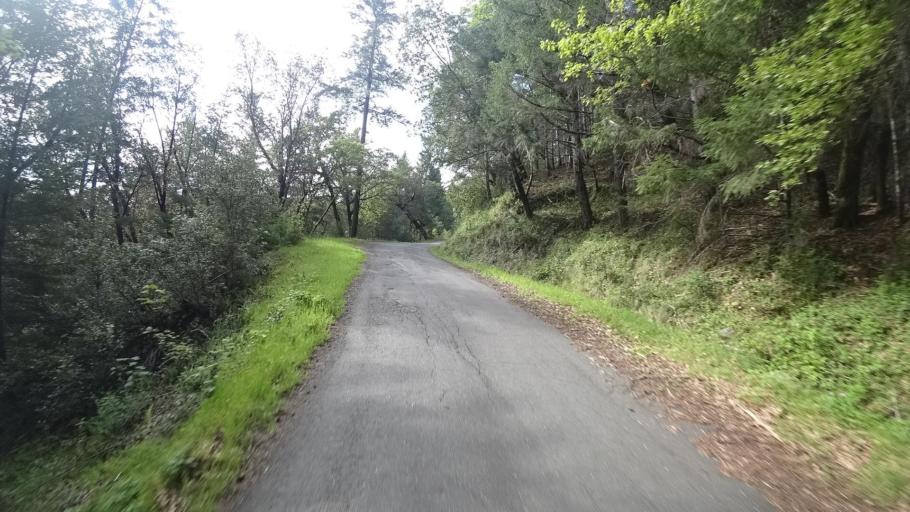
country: US
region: California
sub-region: Humboldt County
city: Redway
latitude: 40.2161
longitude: -123.6578
